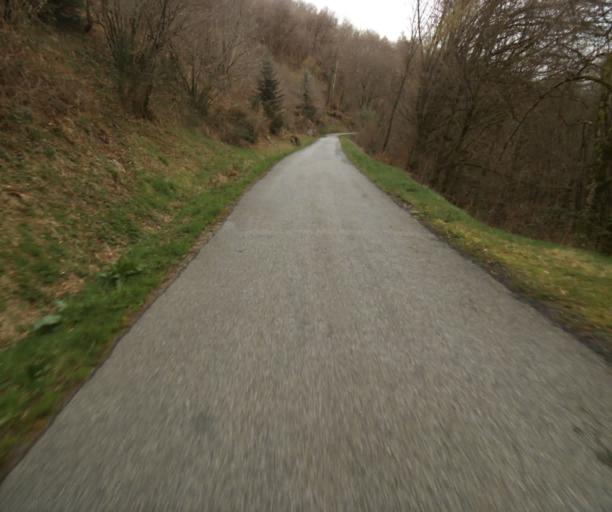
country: FR
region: Limousin
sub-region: Departement de la Correze
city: Argentat
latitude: 45.2311
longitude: 1.9875
